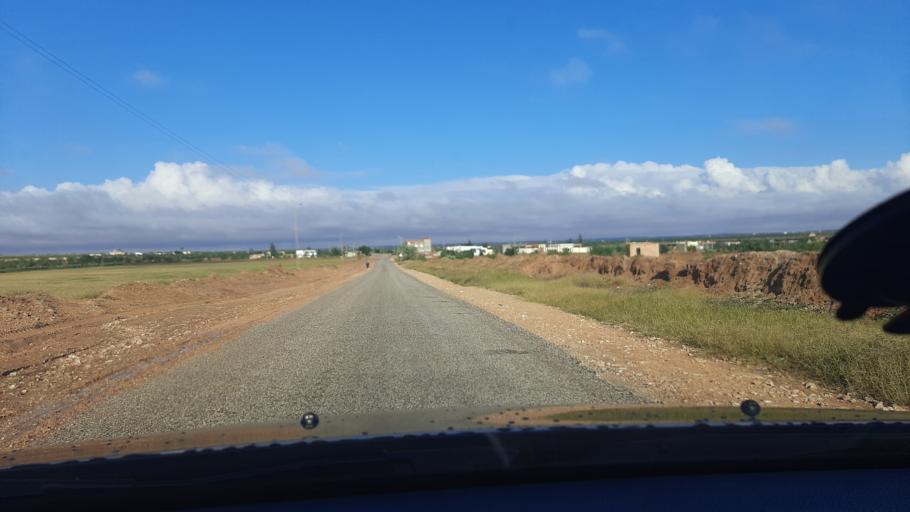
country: TN
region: Safaqis
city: Sfax
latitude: 34.8835
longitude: 10.6295
